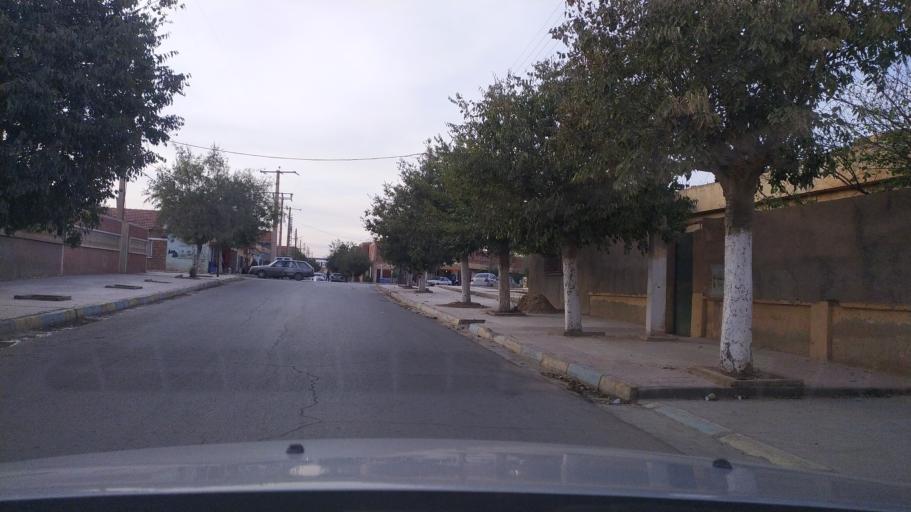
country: DZ
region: Tiaret
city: Frenda
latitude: 34.8992
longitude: 1.2384
